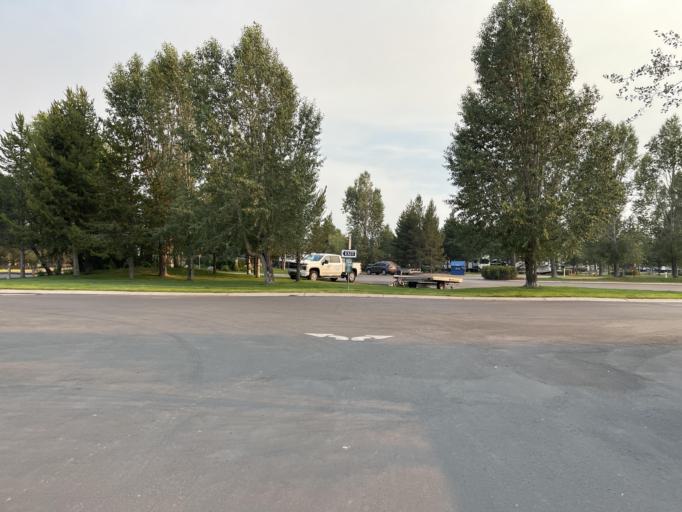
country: US
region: Montana
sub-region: Gallatin County
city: West Yellowstone
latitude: 44.6559
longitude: -111.1046
